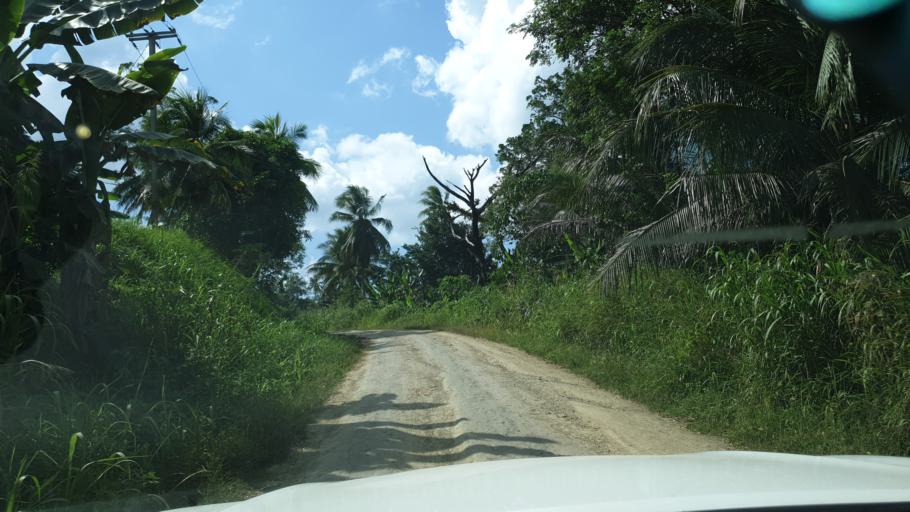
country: PG
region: East Sepik
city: Angoram
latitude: -4.0200
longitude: 144.0621
